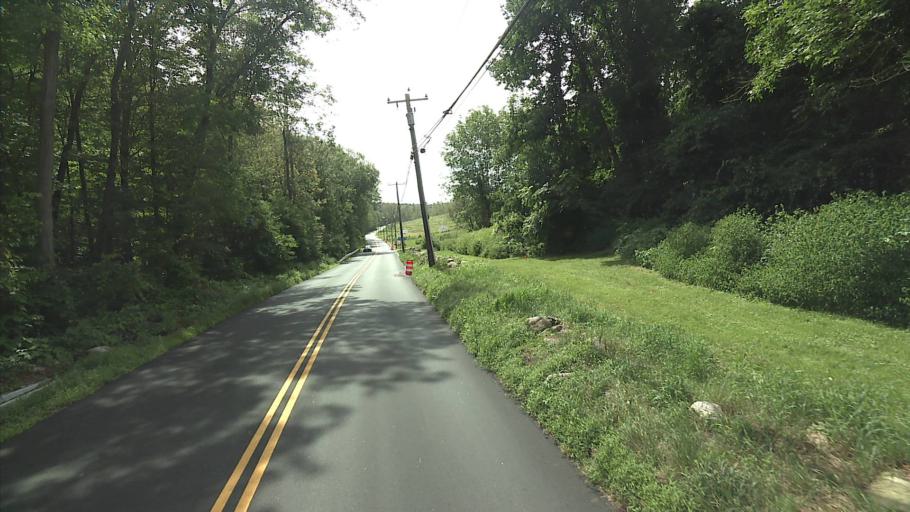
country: US
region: Connecticut
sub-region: Windham County
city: South Woodstock
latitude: 41.9480
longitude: -72.0099
